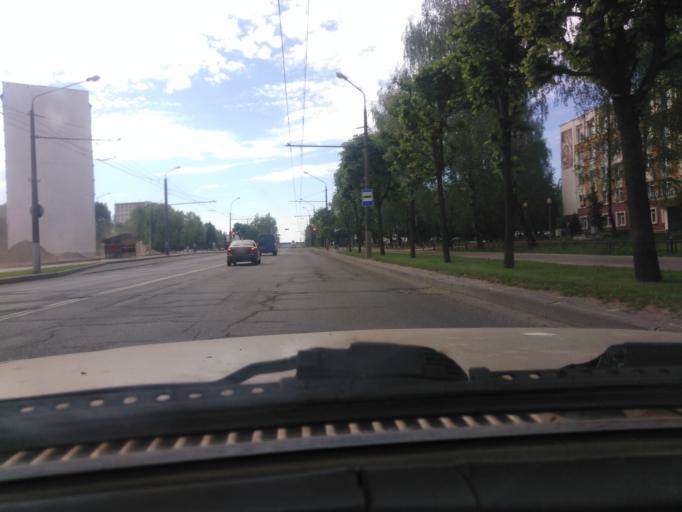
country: BY
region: Mogilev
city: Buynichy
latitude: 53.8957
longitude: 30.2964
